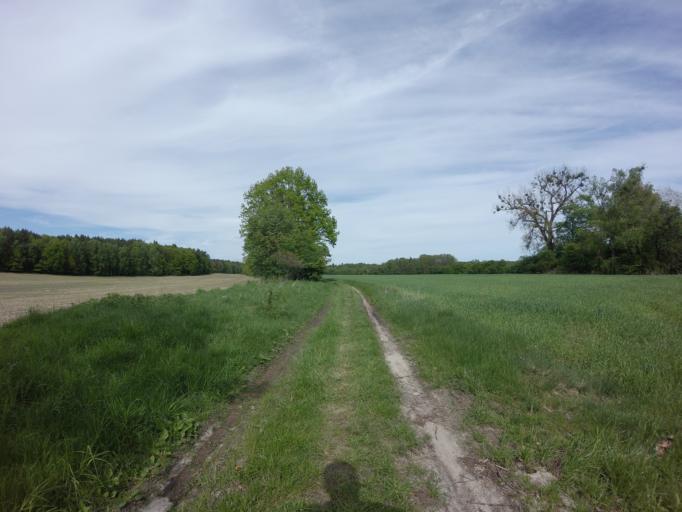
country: PL
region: West Pomeranian Voivodeship
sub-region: Powiat choszczenski
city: Bierzwnik
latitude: 53.1558
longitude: 15.6325
